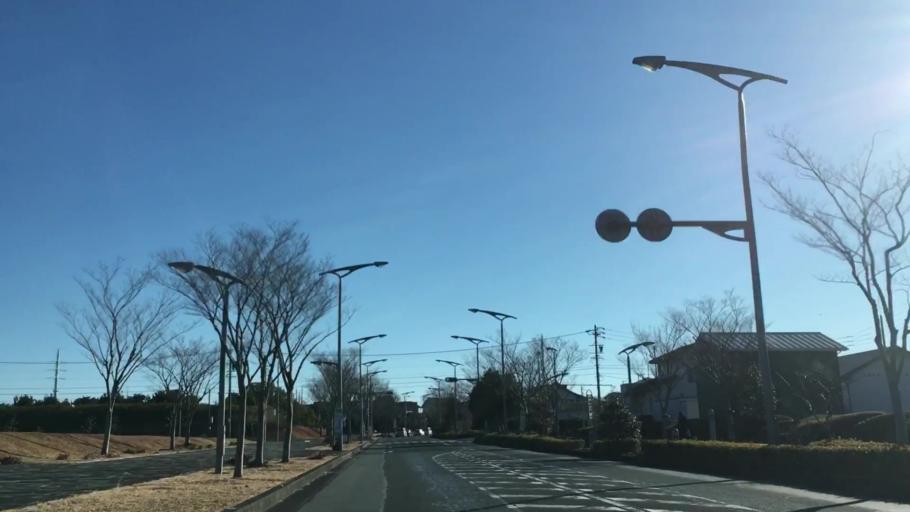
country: JP
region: Shizuoka
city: Hamakita
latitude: 34.8172
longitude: 137.7374
